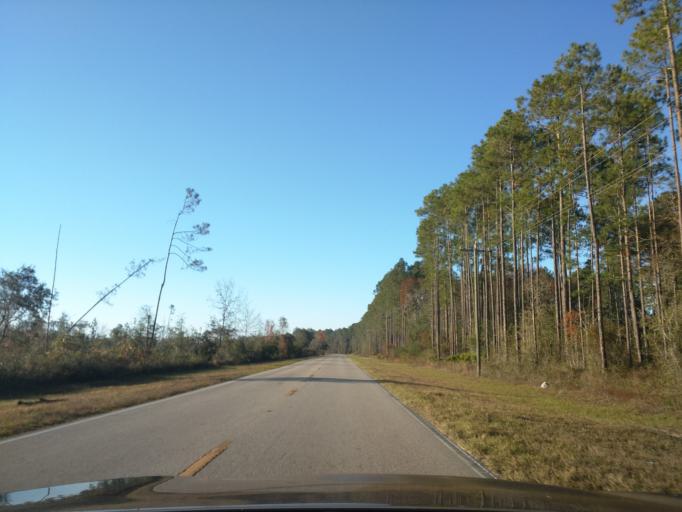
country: US
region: Florida
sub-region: Leon County
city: Woodville
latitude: 30.3470
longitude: -84.1386
